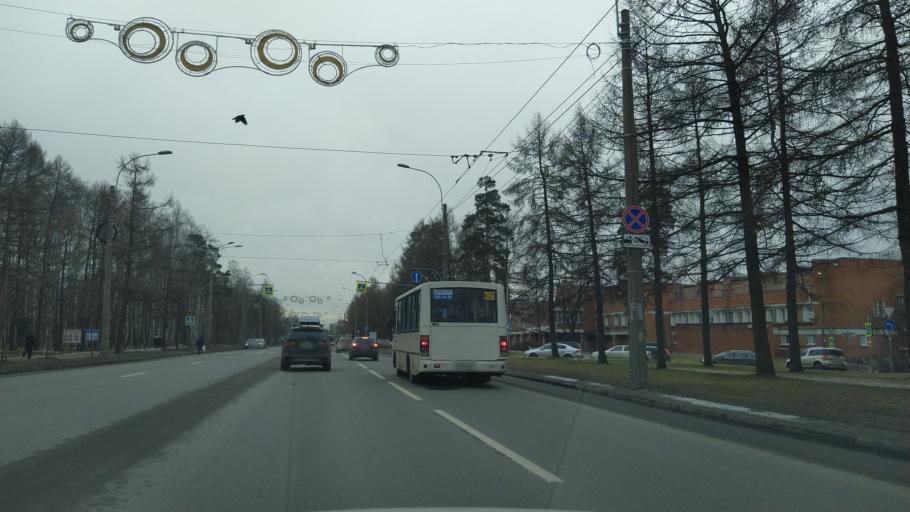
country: RU
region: St.-Petersburg
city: Sosnovka
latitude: 60.0153
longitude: 30.3397
